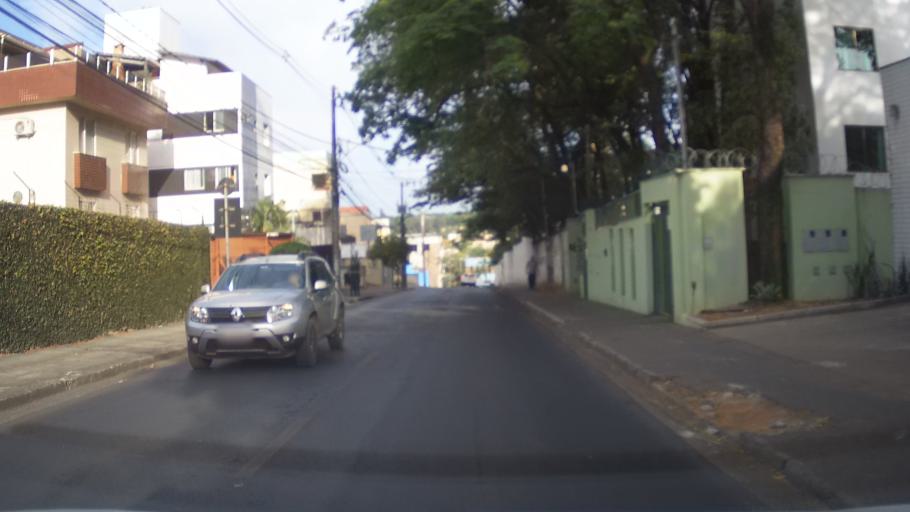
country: BR
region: Minas Gerais
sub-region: Belo Horizonte
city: Belo Horizonte
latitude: -19.8693
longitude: -43.9957
